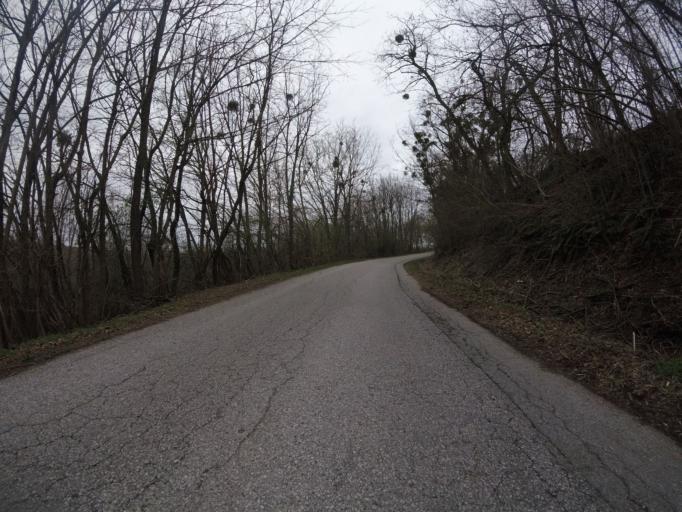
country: HR
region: Zagrebacka
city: Lukavec
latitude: 45.5673
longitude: 15.9697
